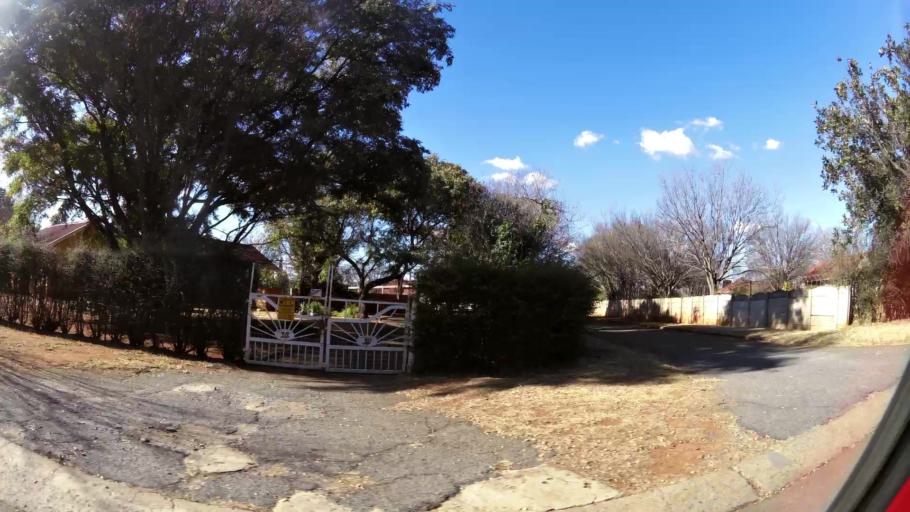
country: ZA
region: Gauteng
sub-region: West Rand District Municipality
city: Carletonville
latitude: -26.3699
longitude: 27.4089
